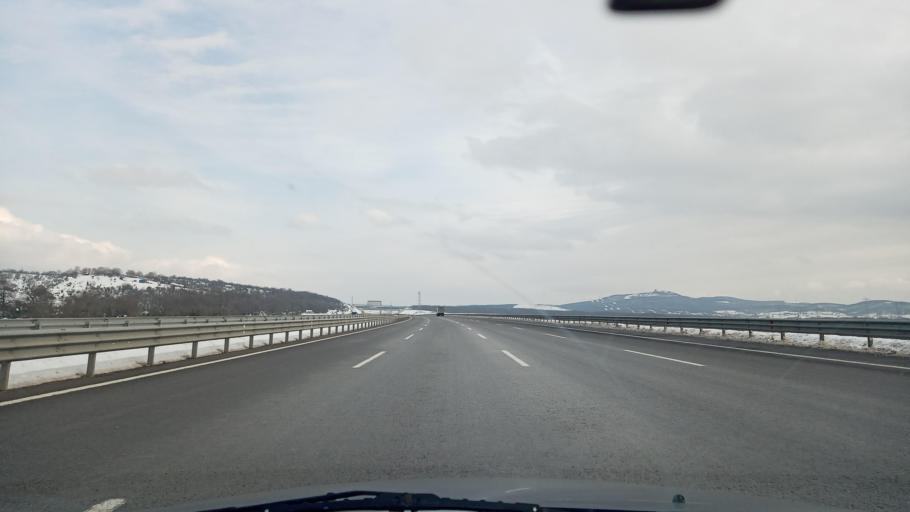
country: TR
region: Kocaeli
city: Mollafeneri
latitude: 40.8885
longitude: 29.5838
